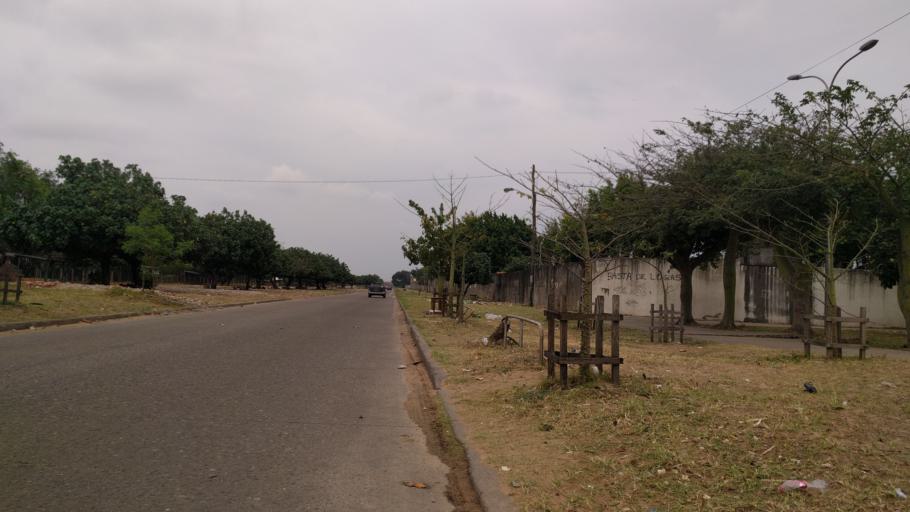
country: BO
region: Santa Cruz
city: Santa Cruz de la Sierra
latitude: -17.8209
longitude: -63.1952
